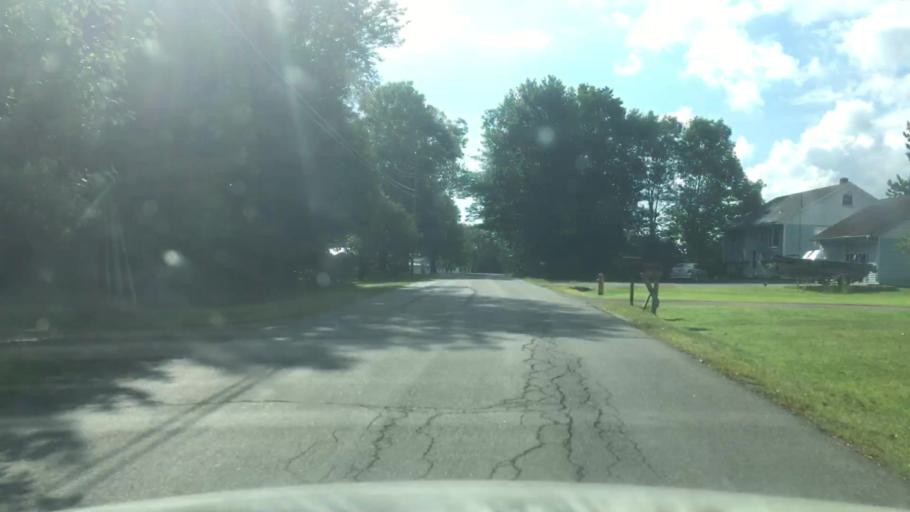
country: US
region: Maine
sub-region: Kennebec County
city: Gardiner
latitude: 44.1710
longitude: -69.8165
